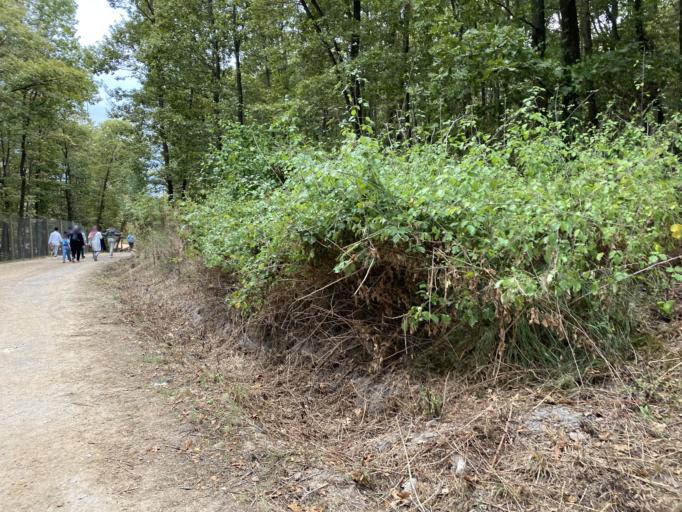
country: TR
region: Kocaeli
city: Derbent
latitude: 40.7375
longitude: 30.1618
